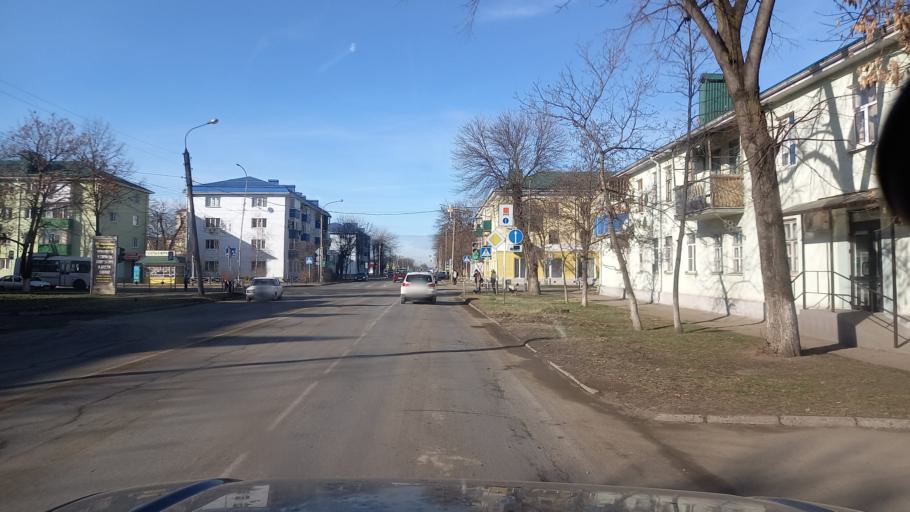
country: RU
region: Adygeya
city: Maykop
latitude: 44.6174
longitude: 40.1077
